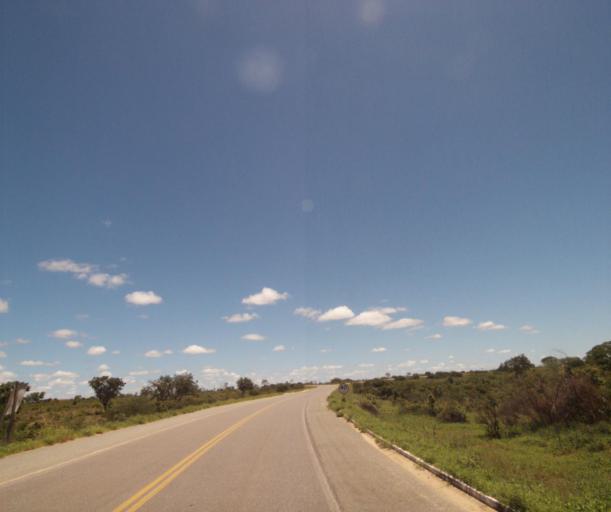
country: BR
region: Bahia
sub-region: Carinhanha
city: Carinhanha
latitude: -14.2899
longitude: -43.7853
